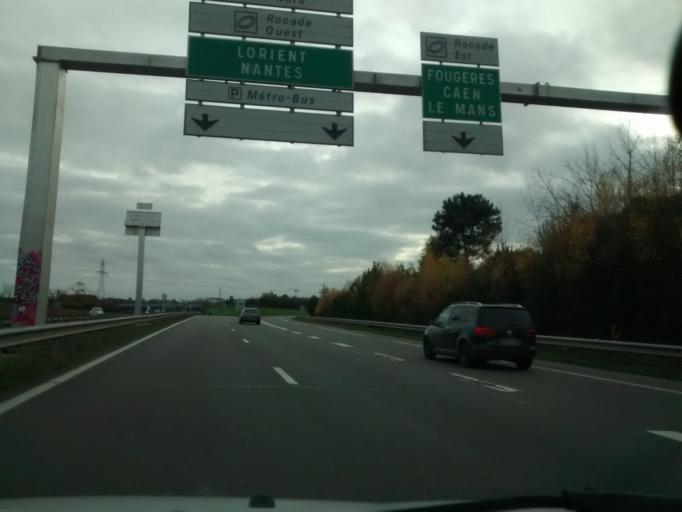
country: FR
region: Brittany
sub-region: Departement d'Ille-et-Vilaine
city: Saint-Gregoire
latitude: 48.1472
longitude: -1.6990
